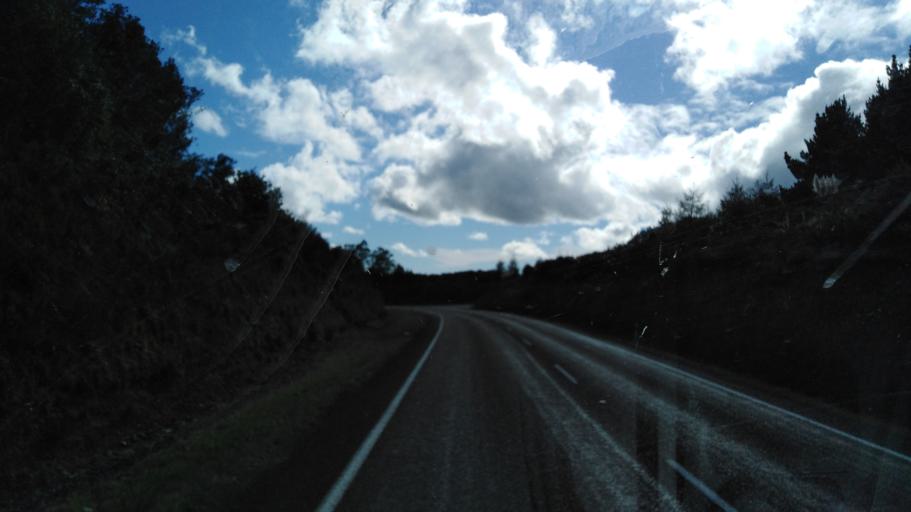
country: NZ
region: Bay of Plenty
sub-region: Rotorua District
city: Rotorua
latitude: -37.9235
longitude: 176.1561
